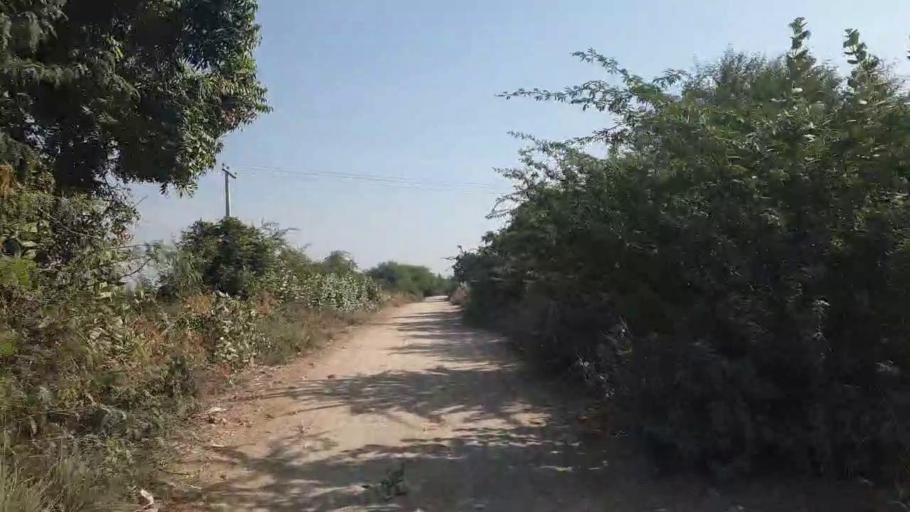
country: PK
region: Sindh
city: Matiari
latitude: 25.6765
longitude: 68.3500
